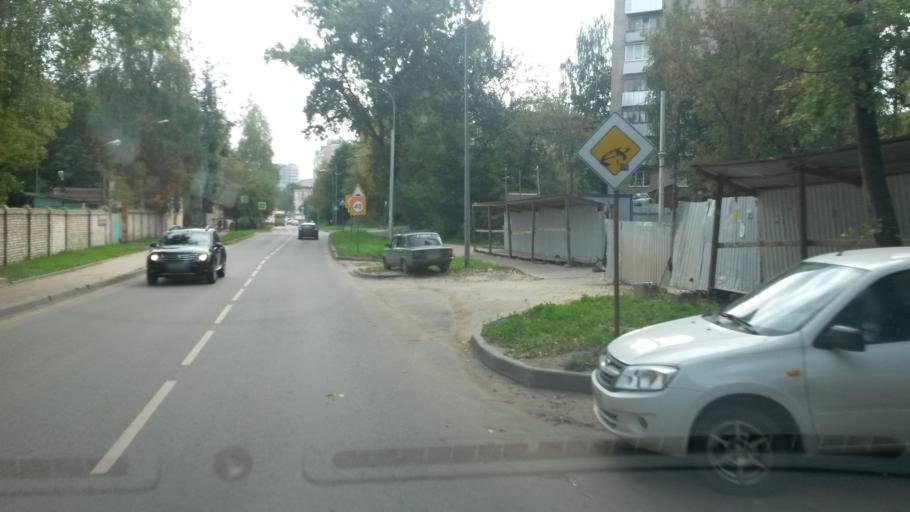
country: RU
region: Ivanovo
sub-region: Gorod Ivanovo
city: Ivanovo
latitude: 57.0048
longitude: 40.9629
